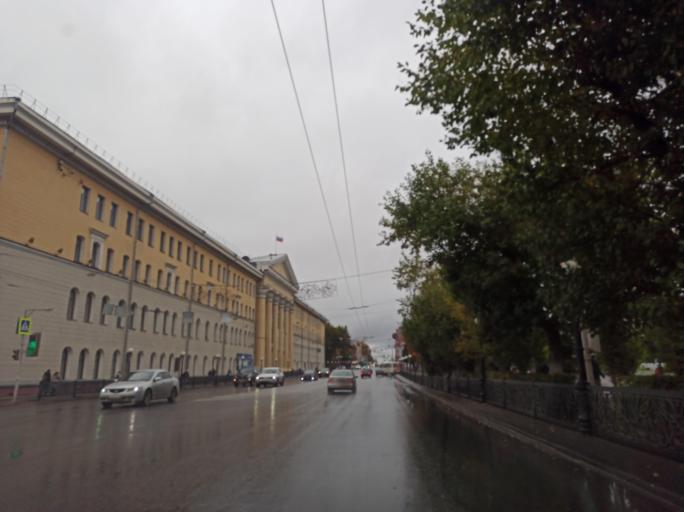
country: RU
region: Tomsk
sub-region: Tomskiy Rayon
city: Tomsk
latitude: 56.4731
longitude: 84.9505
